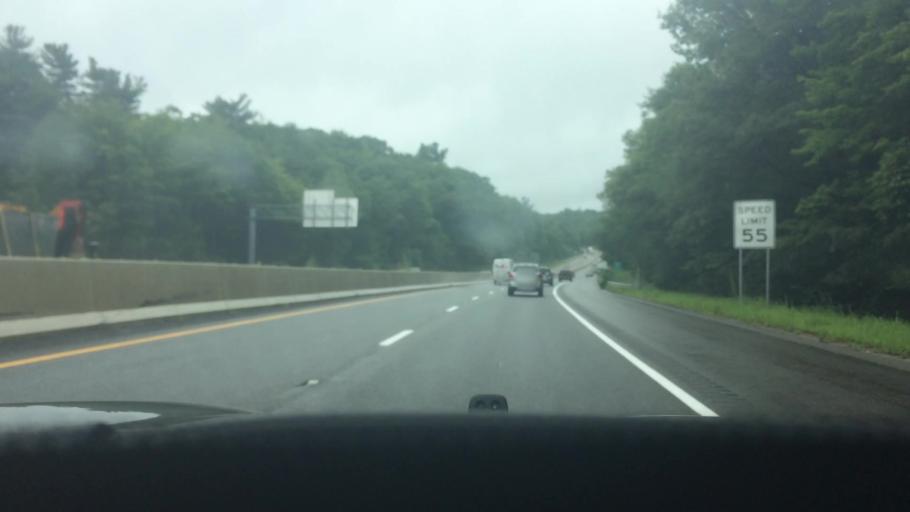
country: US
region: Massachusetts
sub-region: Worcester County
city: Fitchburg
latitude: 42.5515
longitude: -71.7896
